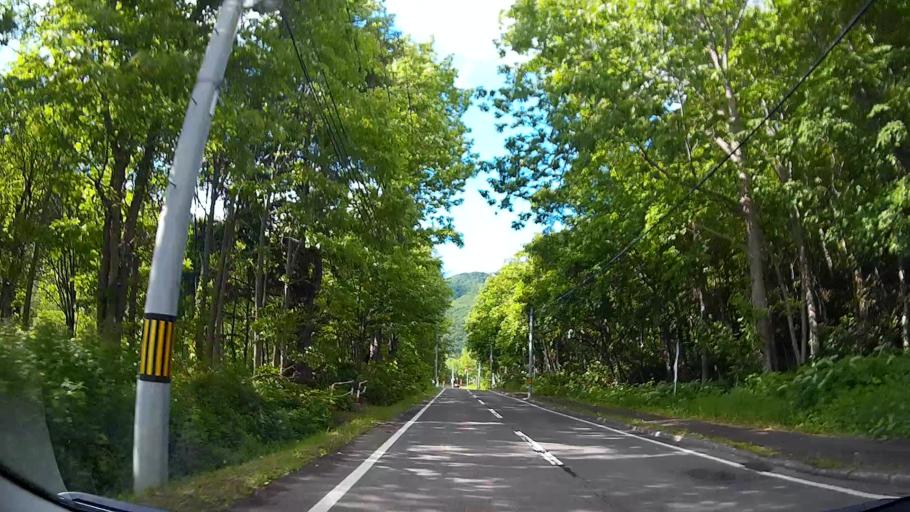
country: JP
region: Hokkaido
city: Sapporo
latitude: 42.9529
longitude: 141.1517
